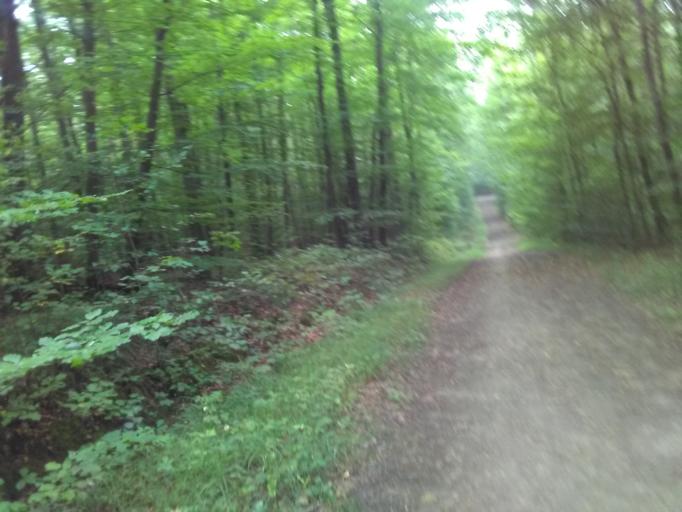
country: DE
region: Bavaria
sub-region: Upper Franconia
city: Bamberg
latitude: 49.8626
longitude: 10.8999
